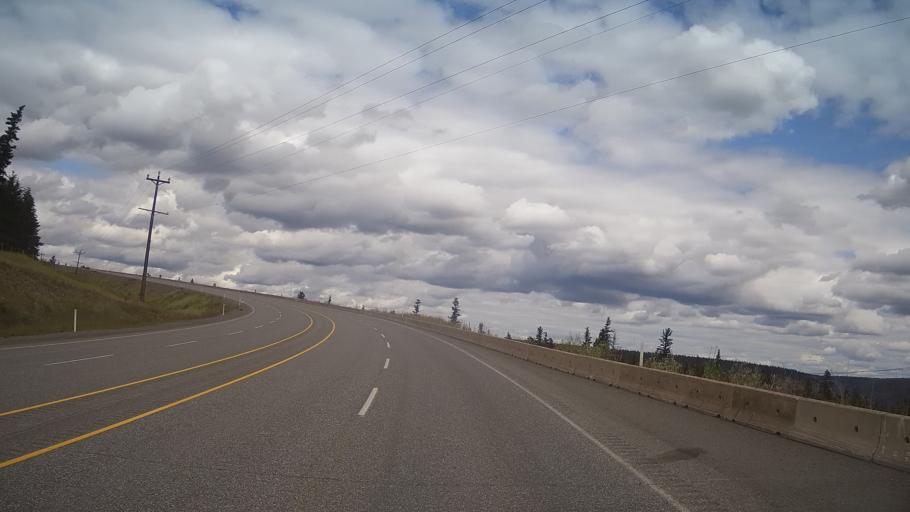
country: CA
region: British Columbia
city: Cache Creek
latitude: 51.1366
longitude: -121.4991
